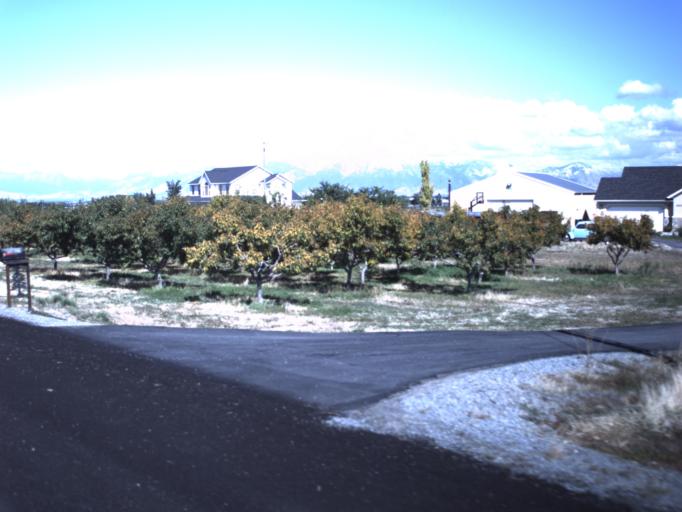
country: US
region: Utah
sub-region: Utah County
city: West Mountain
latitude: 40.0225
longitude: -111.7870
